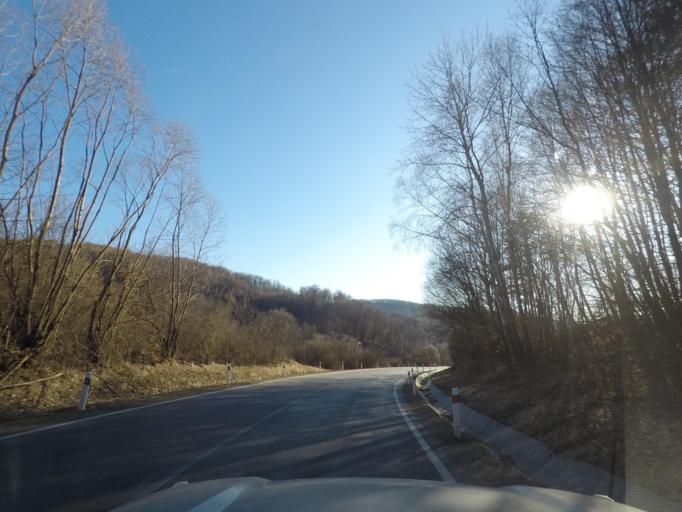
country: SK
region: Presovsky
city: Medzilaborce
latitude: 49.2841
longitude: 21.8477
